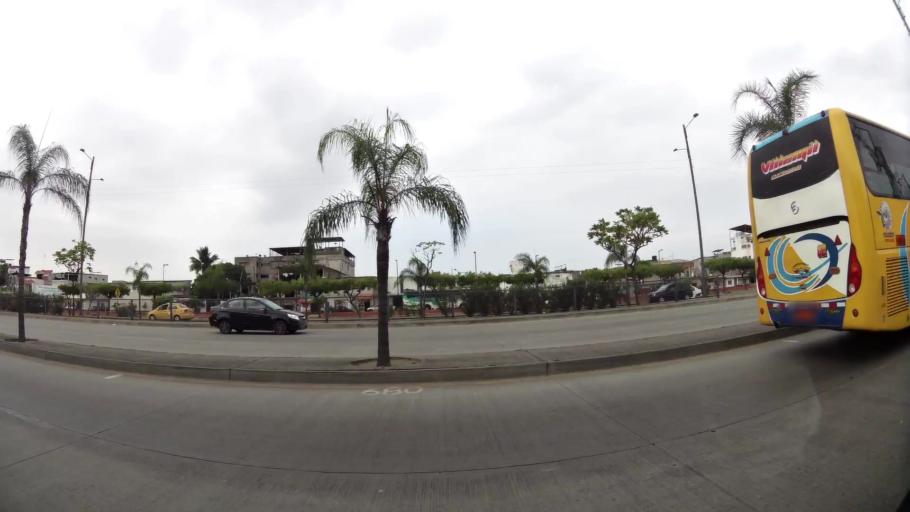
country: EC
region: Guayas
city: Eloy Alfaro
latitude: -2.1330
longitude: -79.8822
